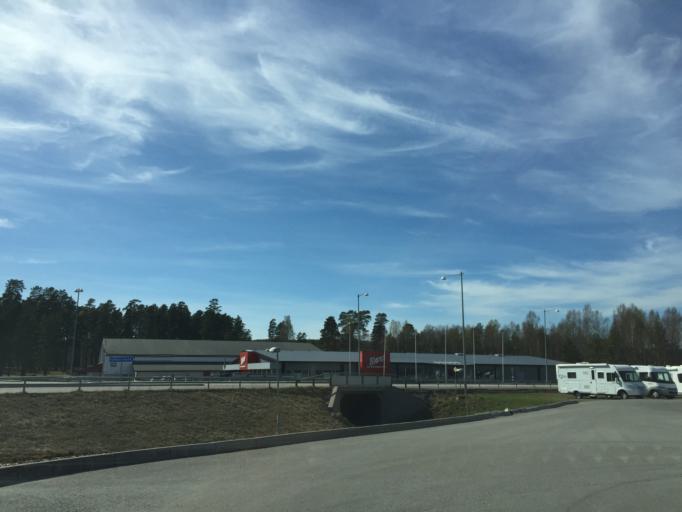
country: SE
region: Vaermland
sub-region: Eda Kommun
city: Charlottenberg
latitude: 59.8796
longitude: 12.2875
